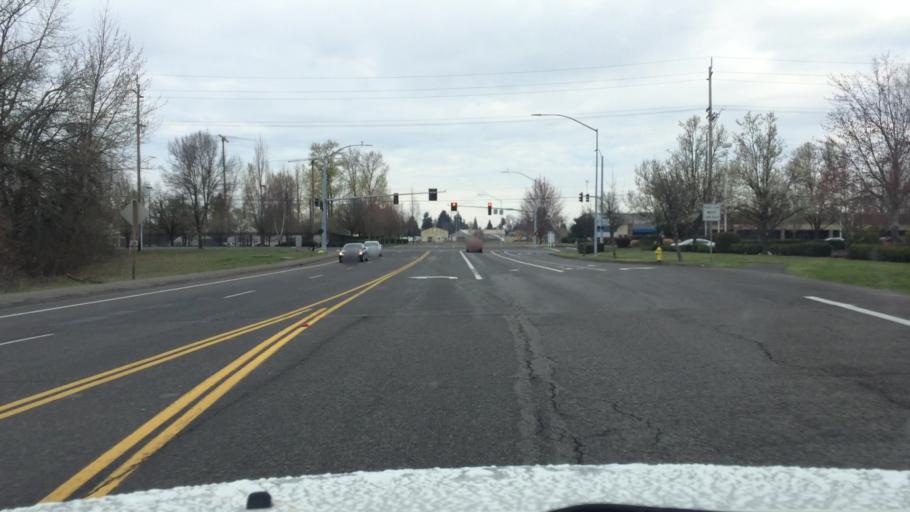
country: US
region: Oregon
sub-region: Marion County
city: Four Corners
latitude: 44.9269
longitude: -122.9937
